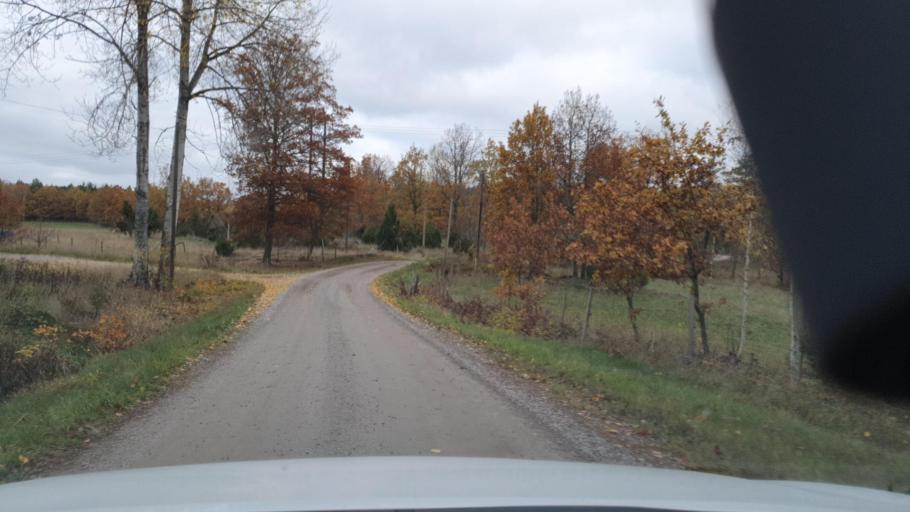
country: SE
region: Kalmar
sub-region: Vasterviks Kommun
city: Vaestervik
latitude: 57.7267
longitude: 16.4800
